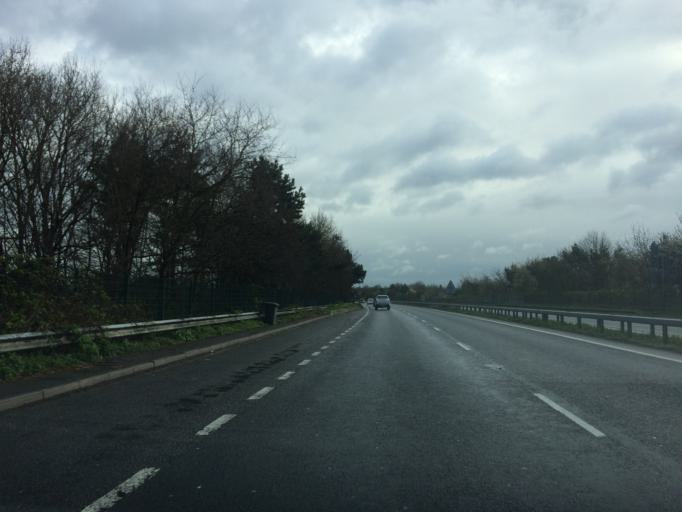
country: GB
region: England
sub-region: Surrey
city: Addlestone
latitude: 51.3756
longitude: -0.5054
